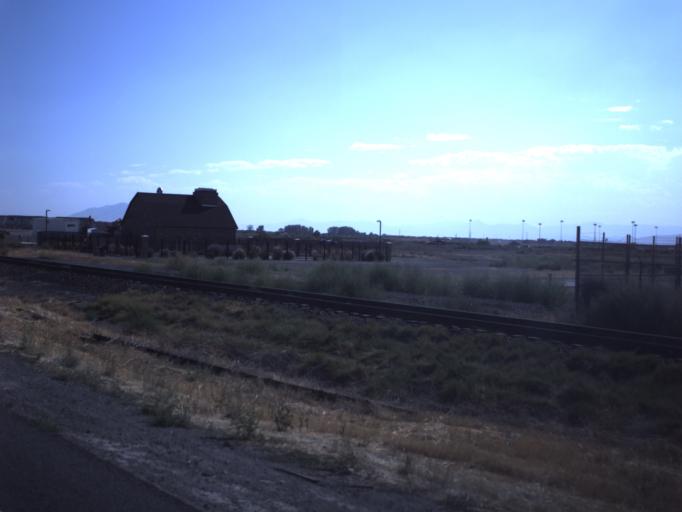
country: US
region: Utah
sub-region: Utah County
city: Lindon
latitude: 40.3135
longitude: -111.7350
